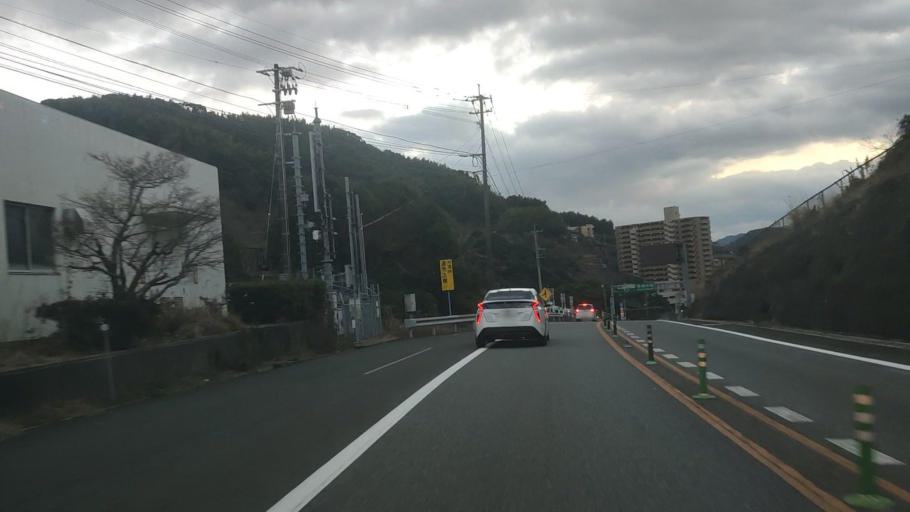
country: JP
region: Nagasaki
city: Nagasaki-shi
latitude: 32.7709
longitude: 129.8910
